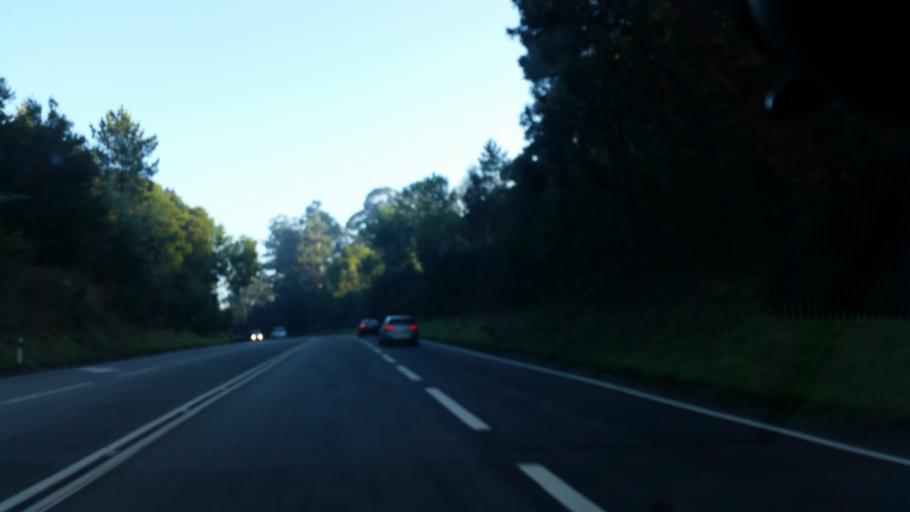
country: PT
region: Porto
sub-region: Santo Tirso
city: Sao Miguel do Couto
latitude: 41.3338
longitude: -8.4682
